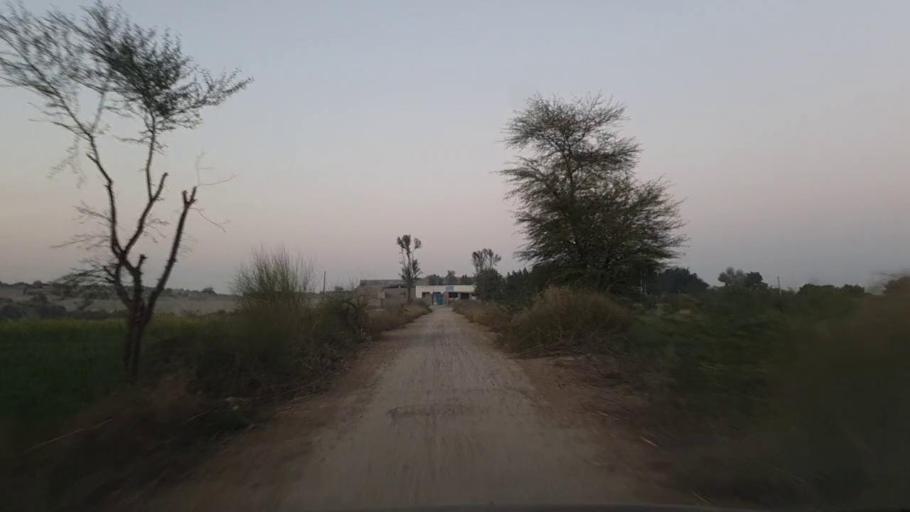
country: PK
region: Sindh
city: Daur
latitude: 26.4837
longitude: 68.4835
